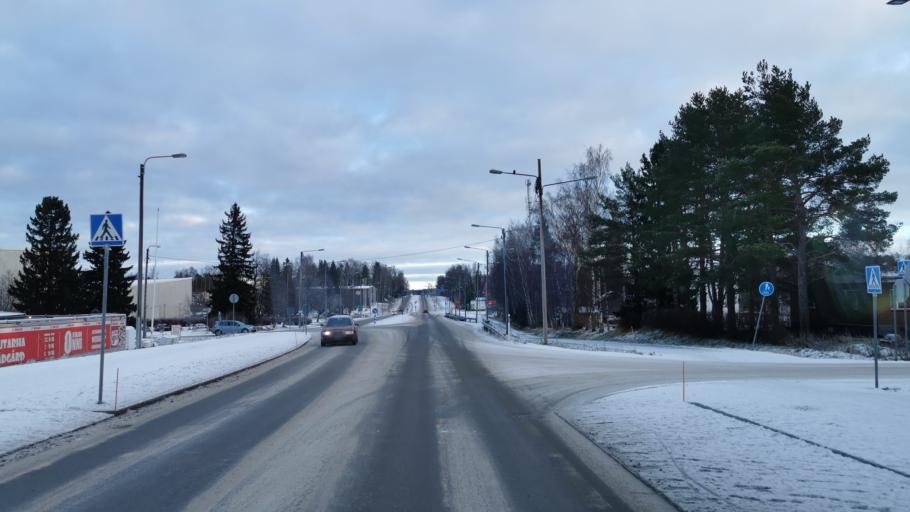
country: FI
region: Ostrobothnia
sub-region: Vaasa
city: Korsholm
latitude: 63.1138
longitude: 21.6811
